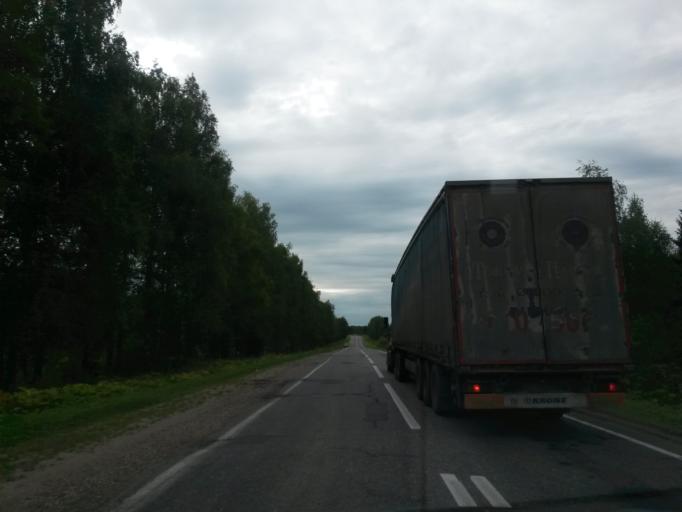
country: RU
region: Jaroslavl
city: Gavrilov-Yam
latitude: 57.3646
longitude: 39.7423
